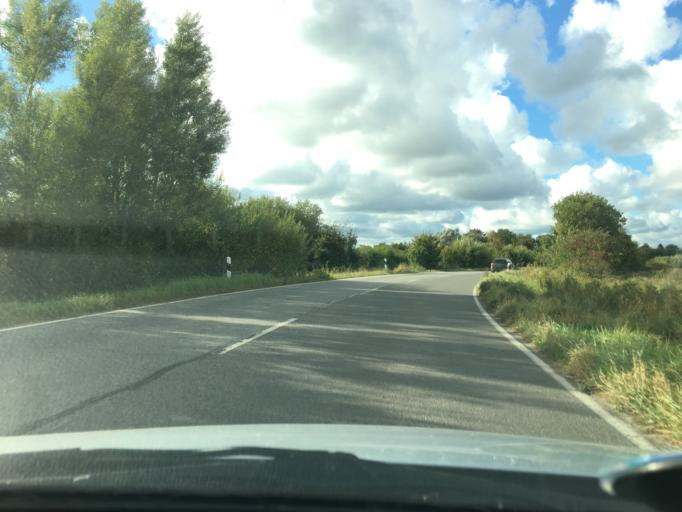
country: DE
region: Schleswig-Holstein
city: Wendtorf
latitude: 54.4164
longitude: 10.2910
